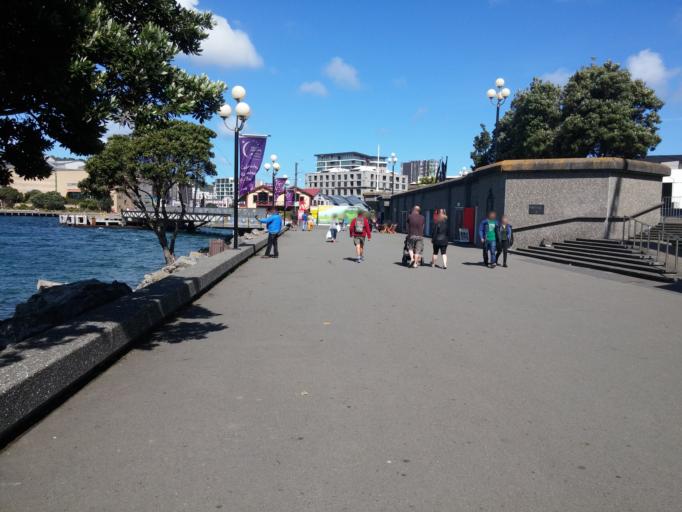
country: NZ
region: Wellington
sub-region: Wellington City
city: Wellington
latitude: -41.2873
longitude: 174.7793
